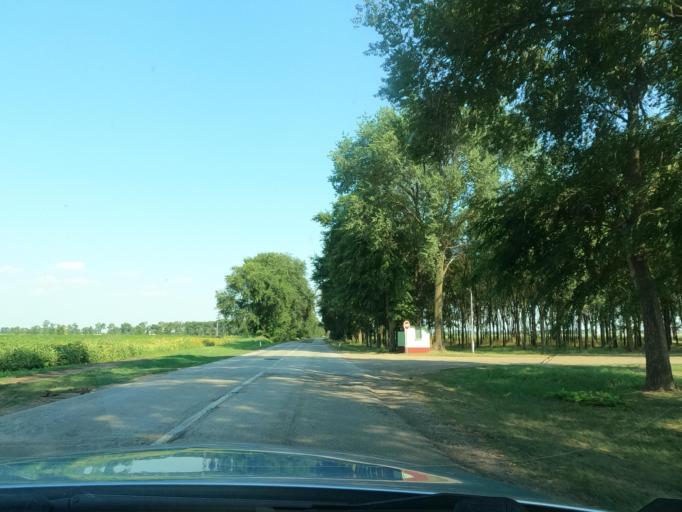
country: RS
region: Autonomna Pokrajina Vojvodina
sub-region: Juznobacki Okrug
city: Becej
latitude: 45.6672
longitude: 19.9330
